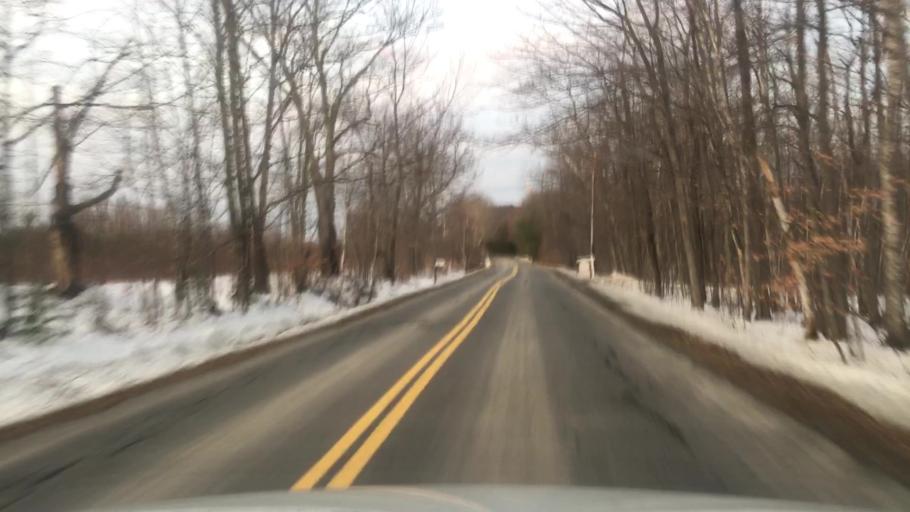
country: US
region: Maine
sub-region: Somerset County
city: Canaan
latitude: 44.7501
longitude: -69.6298
